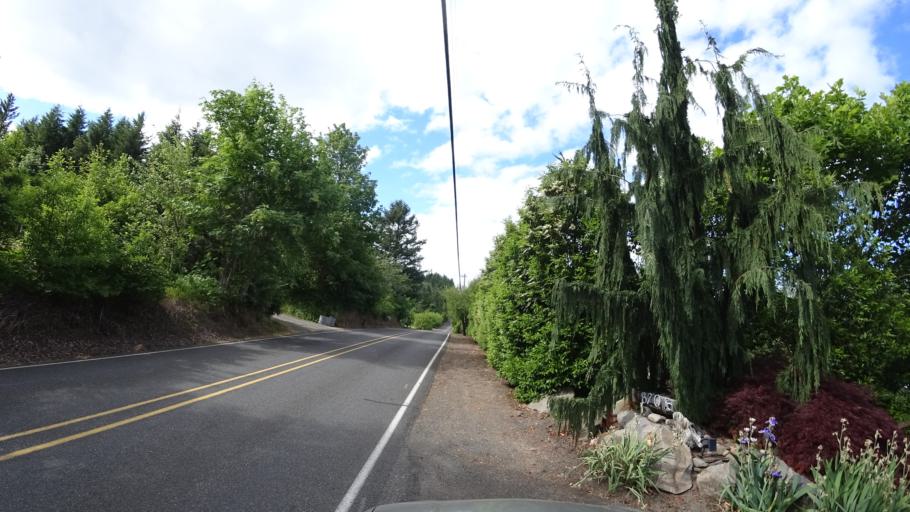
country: US
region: Oregon
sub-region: Washington County
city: Bethany
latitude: 45.5861
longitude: -122.8418
